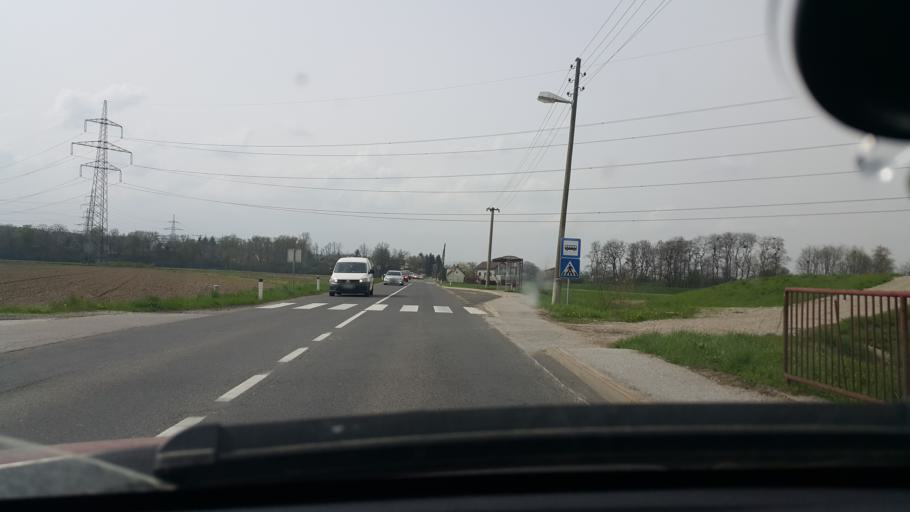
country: SI
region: Duplek
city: Zgornji Duplek
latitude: 46.5171
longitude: 15.7091
